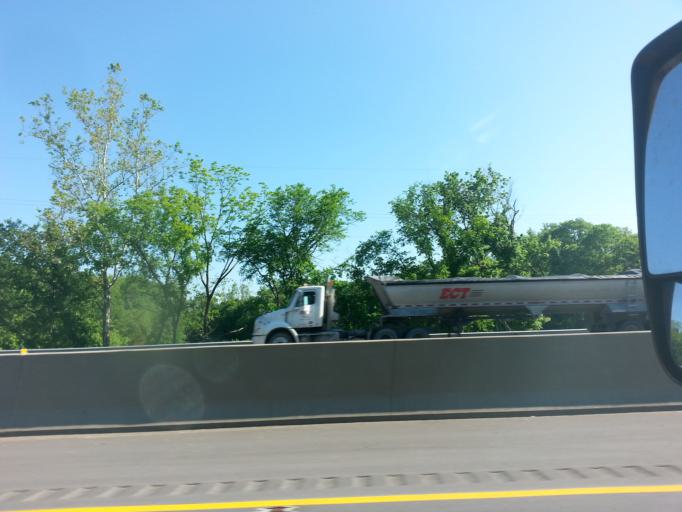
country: US
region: Kentucky
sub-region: Shelby County
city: Simpsonville
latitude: 38.2028
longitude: -85.3170
